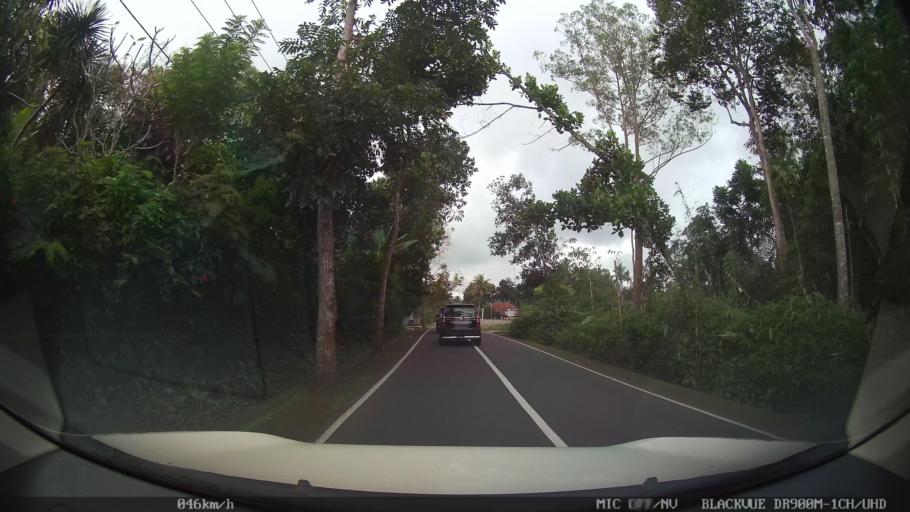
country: ID
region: Bali
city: Banjar Bias
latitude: -8.3765
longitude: 115.4184
